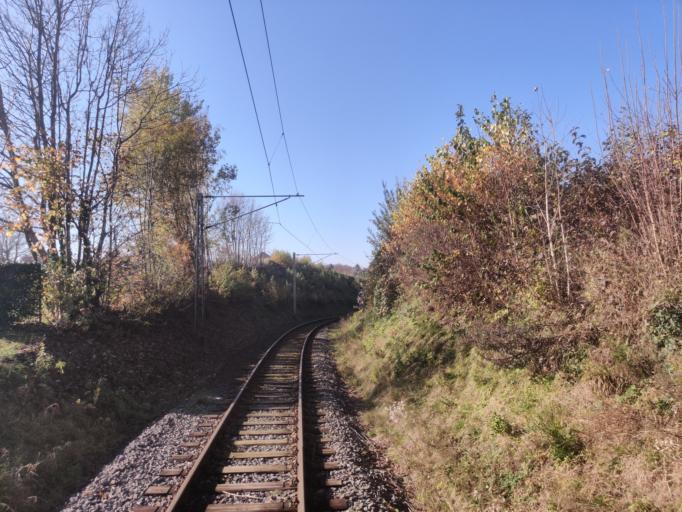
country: AT
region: Styria
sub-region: Politischer Bezirk Suedoststeiermark
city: Maierdorf
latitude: 46.8931
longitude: 15.8727
